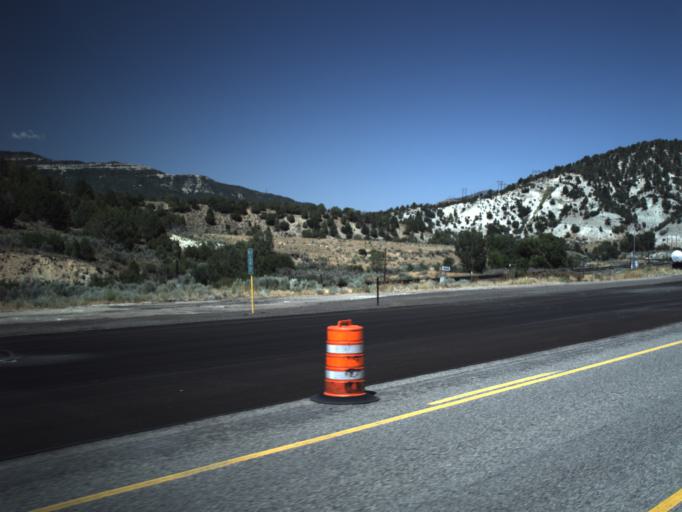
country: US
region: Utah
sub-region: Utah County
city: Mapleton
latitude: 39.9616
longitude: -111.3050
